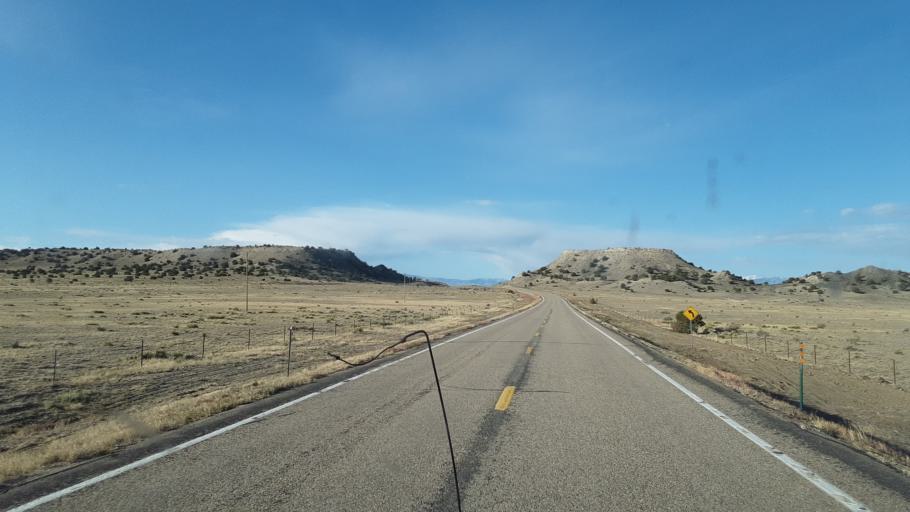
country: US
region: Colorado
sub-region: Huerfano County
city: Walsenburg
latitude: 37.6952
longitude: -104.6239
